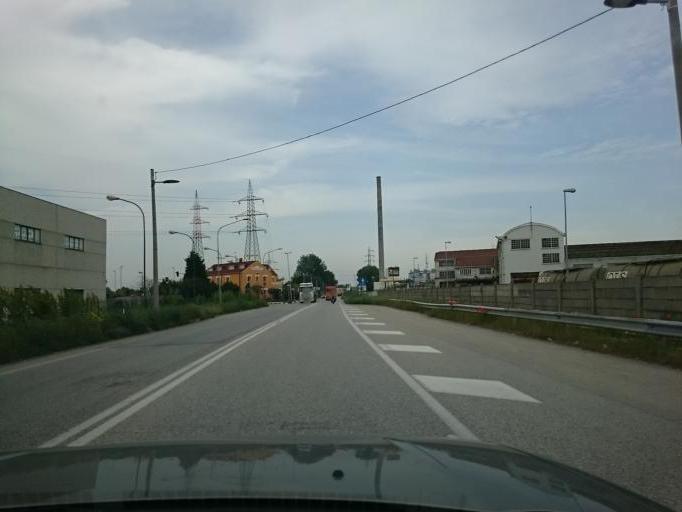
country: IT
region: Veneto
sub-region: Provincia di Venezia
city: Mestre
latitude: 45.4555
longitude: 12.2165
